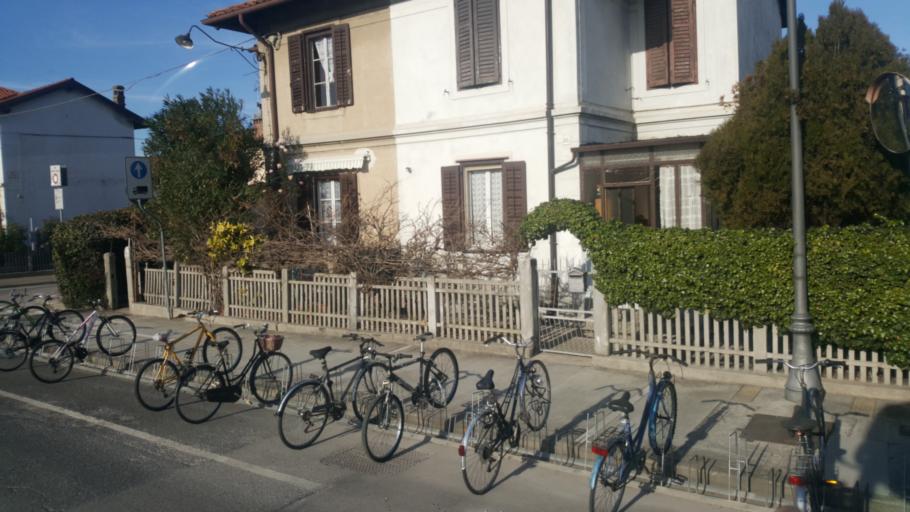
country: IT
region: Friuli Venezia Giulia
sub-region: Provincia di Gorizia
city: Monfalcone
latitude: 45.7946
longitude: 13.5350
